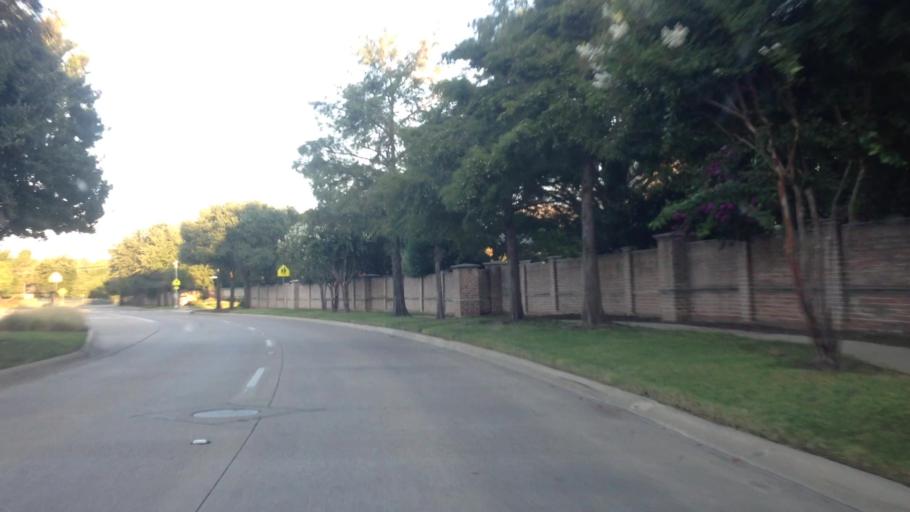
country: US
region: Texas
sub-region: Tarrant County
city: Southlake
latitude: 32.9282
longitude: -97.1296
